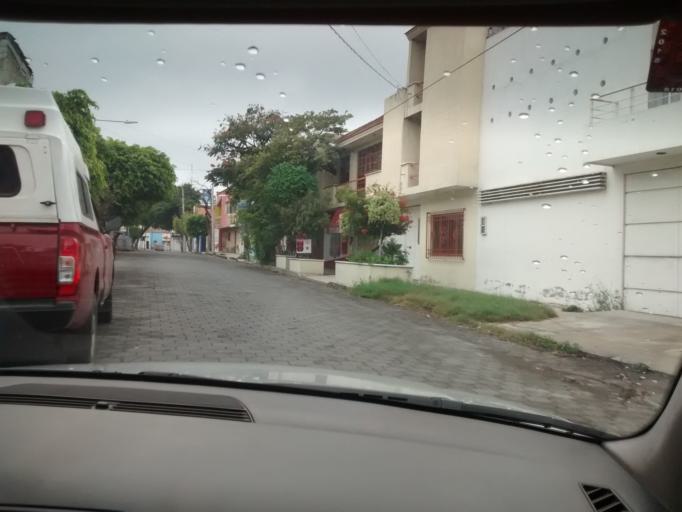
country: MX
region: Puebla
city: Tehuacan
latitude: 18.4601
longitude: -97.3991
